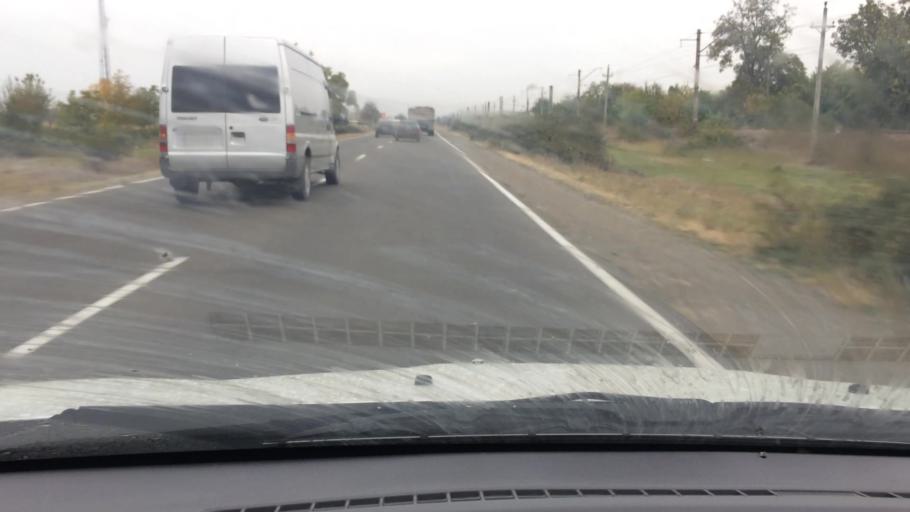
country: GE
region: Kvemo Kartli
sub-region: Marneuli
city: Marneuli
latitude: 41.4325
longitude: 44.8206
